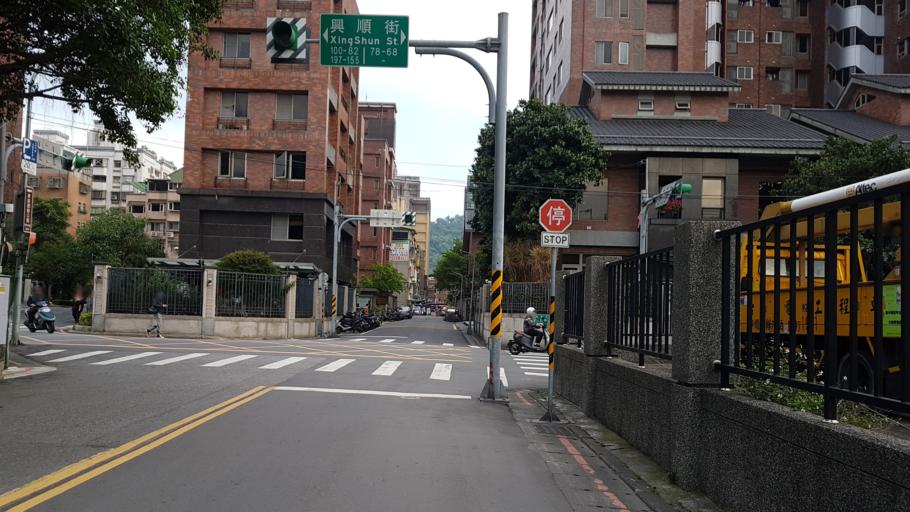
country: TW
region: Taipei
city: Taipei
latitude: 25.0014
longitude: 121.5448
